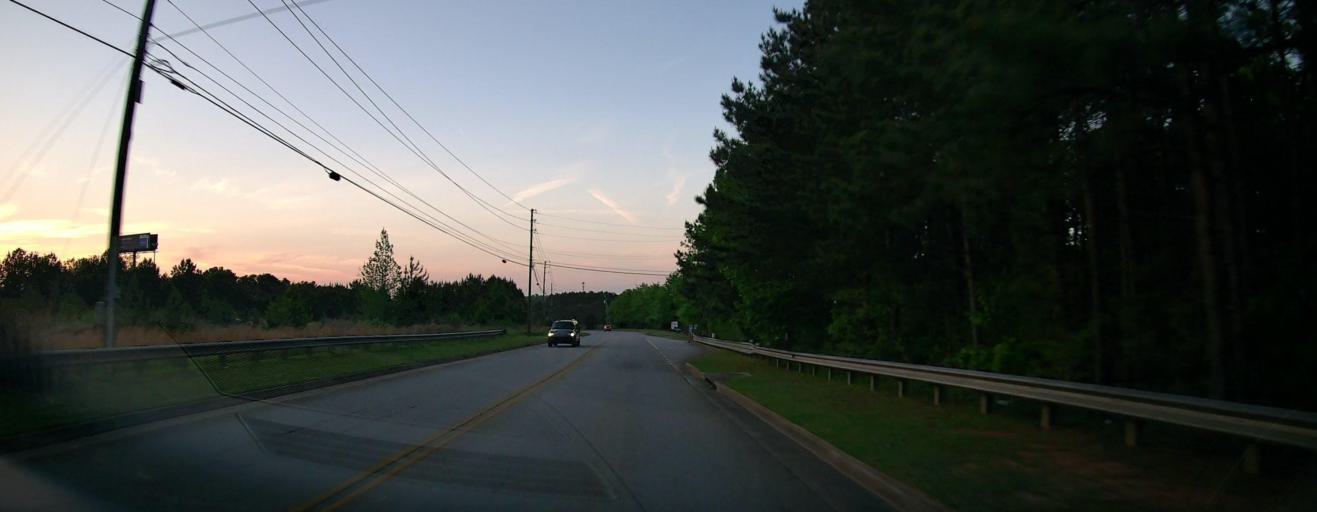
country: US
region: Georgia
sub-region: Henry County
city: Stockbridge
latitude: 33.4921
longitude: -84.2177
